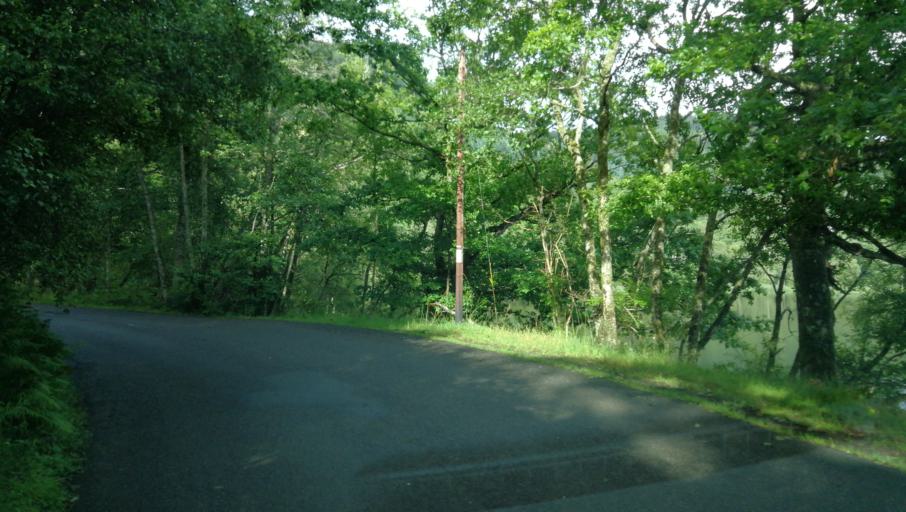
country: GB
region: Scotland
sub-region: Stirling
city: Balfron
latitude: 56.2313
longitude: -4.4105
